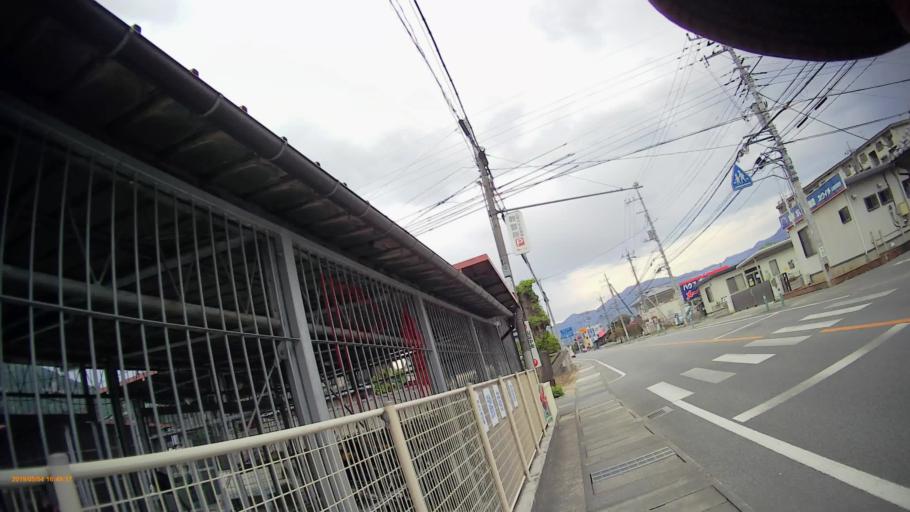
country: JP
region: Yamanashi
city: Isawa
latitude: 35.6544
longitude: 138.6114
